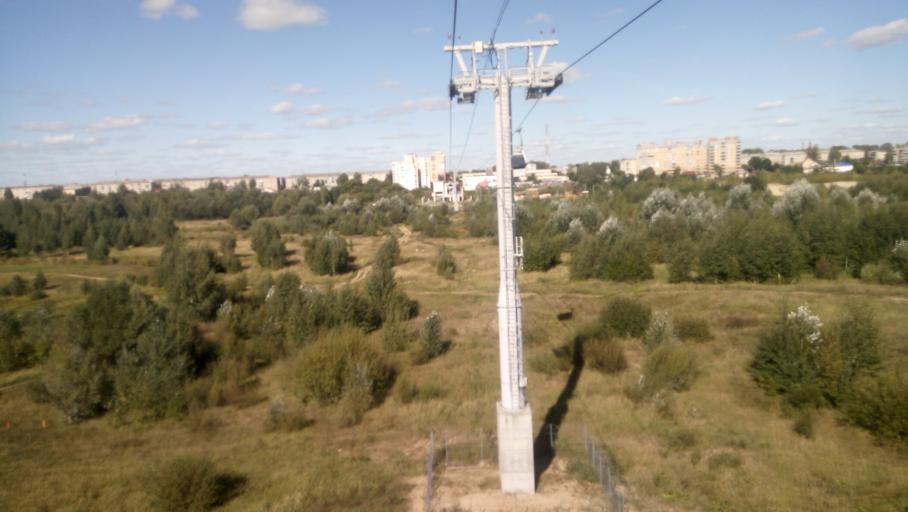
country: RU
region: Nizjnij Novgorod
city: Bor
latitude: 56.3495
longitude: 44.0578
